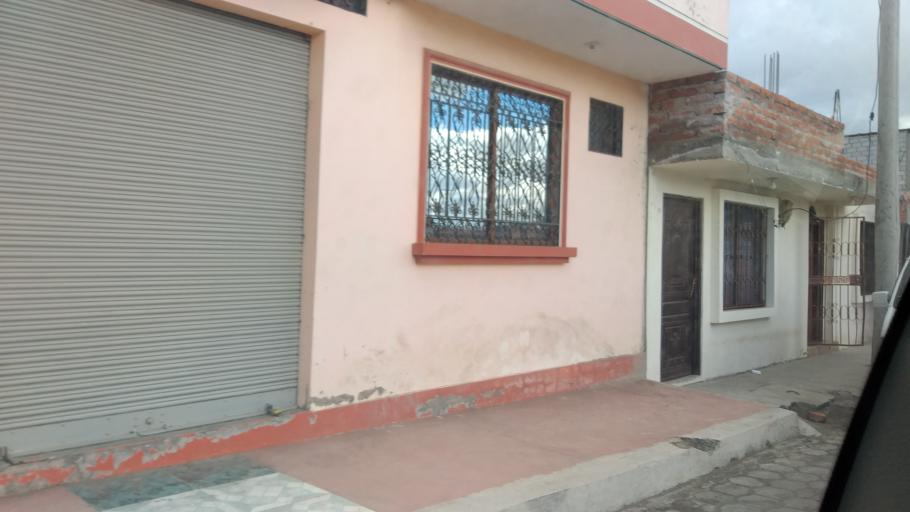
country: EC
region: Chimborazo
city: Riobamba
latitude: -1.6893
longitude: -78.6287
